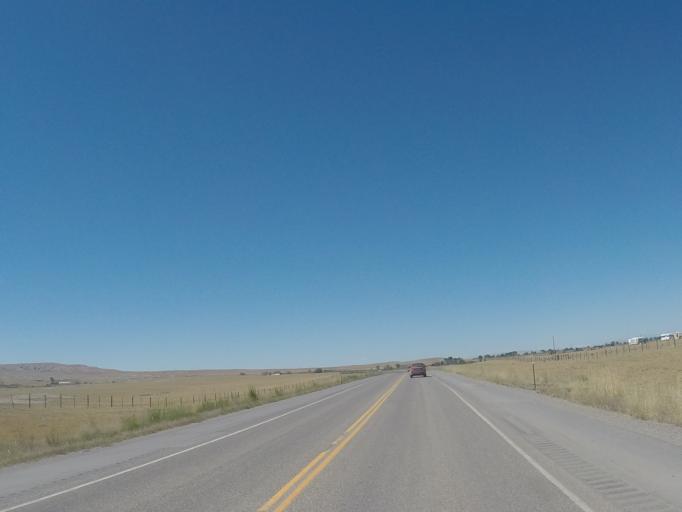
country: US
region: Wyoming
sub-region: Big Horn County
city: Greybull
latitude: 44.5026
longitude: -107.9682
